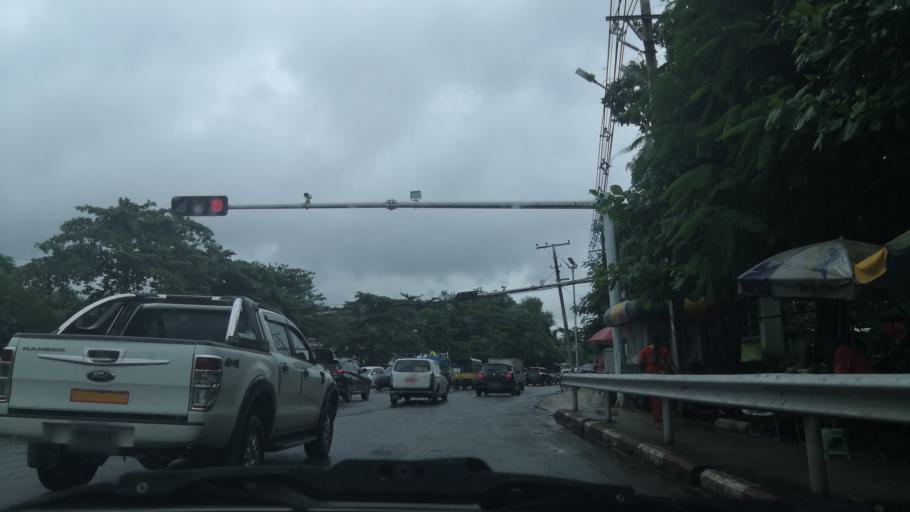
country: MM
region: Yangon
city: Yangon
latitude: 16.8931
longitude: 96.1201
